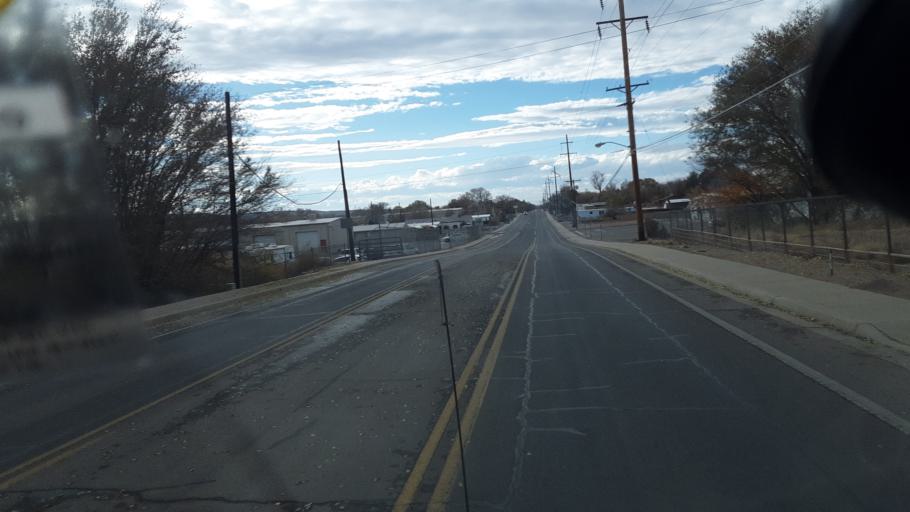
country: US
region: New Mexico
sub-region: San Juan County
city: Farmington
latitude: 36.7265
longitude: -108.1675
